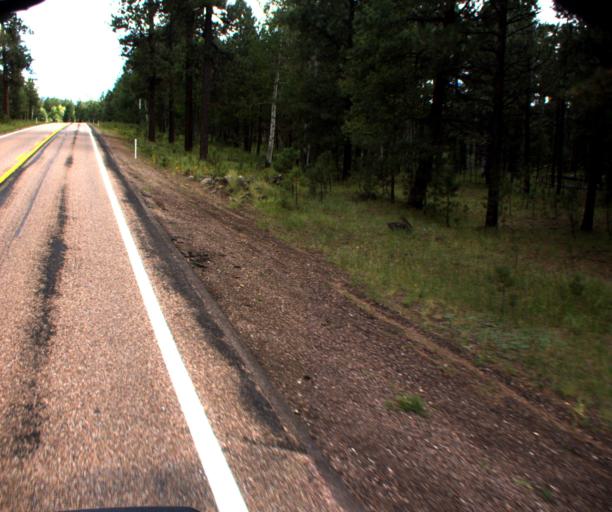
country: US
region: Arizona
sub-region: Navajo County
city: Pinetop-Lakeside
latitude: 34.0309
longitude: -109.6602
